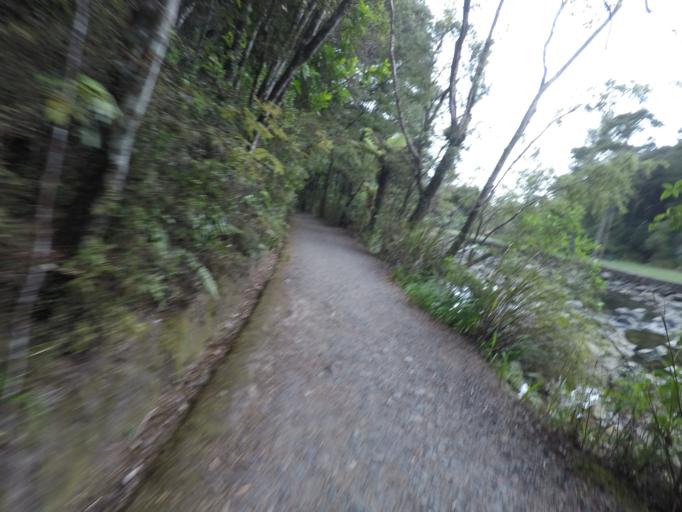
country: NZ
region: Northland
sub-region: Whangarei
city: Whangarei
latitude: -35.7116
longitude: 174.3301
